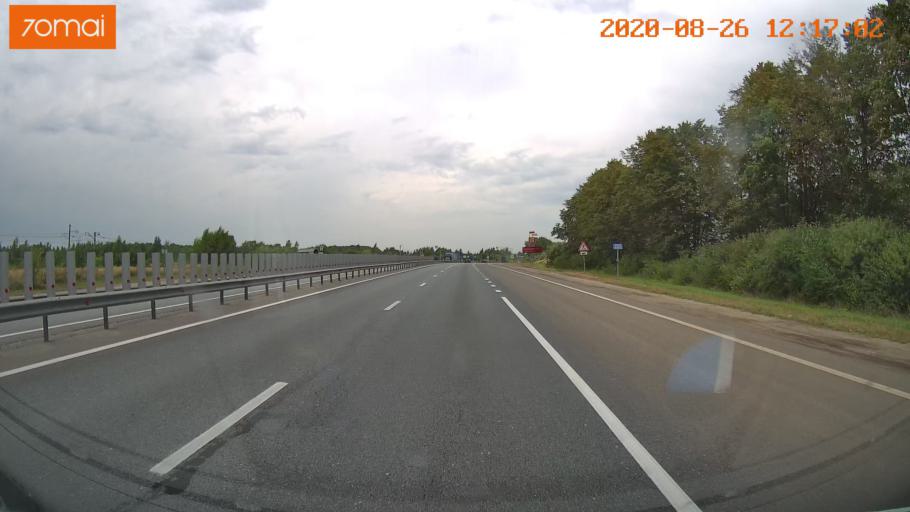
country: RU
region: Rjazan
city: Murmino
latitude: 54.4553
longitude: 40.0332
